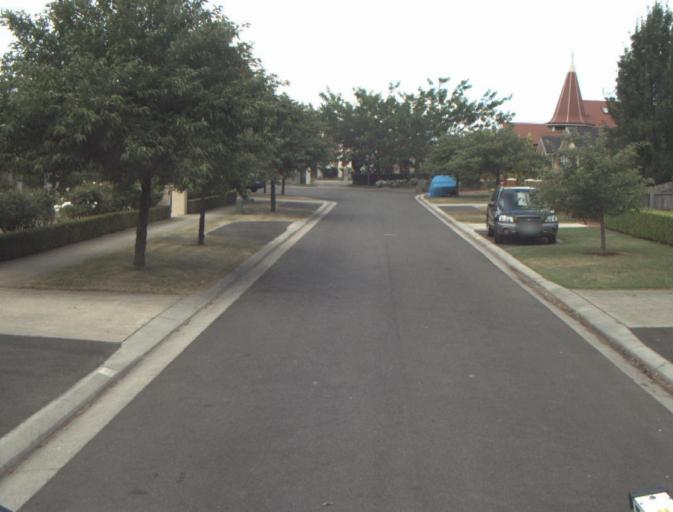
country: AU
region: Tasmania
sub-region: Launceston
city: East Launceston
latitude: -41.4341
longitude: 147.1572
